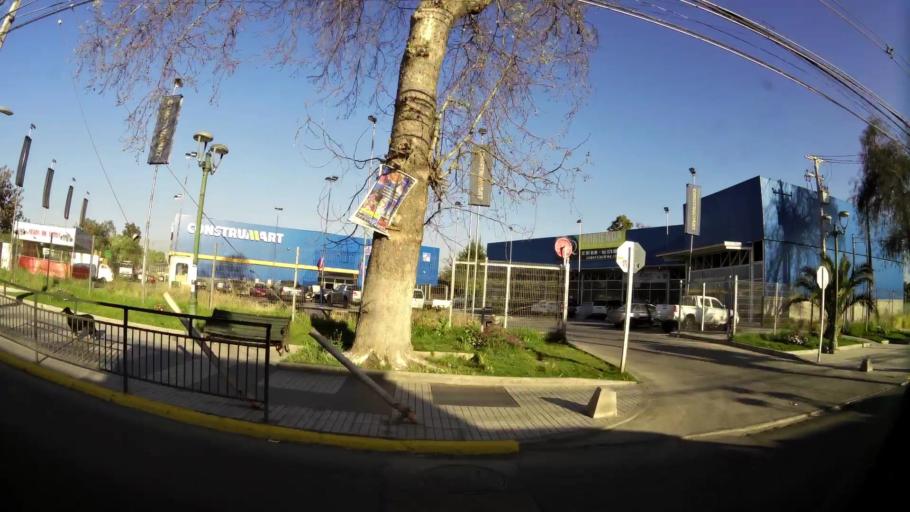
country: CL
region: Santiago Metropolitan
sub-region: Provincia de Talagante
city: Penaflor
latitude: -33.6051
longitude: -70.8530
